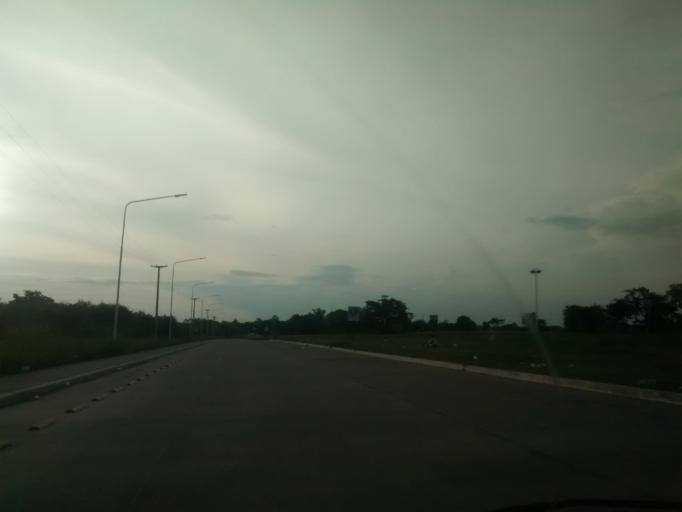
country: AR
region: Chaco
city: Resistencia
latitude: -27.4334
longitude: -58.9701
